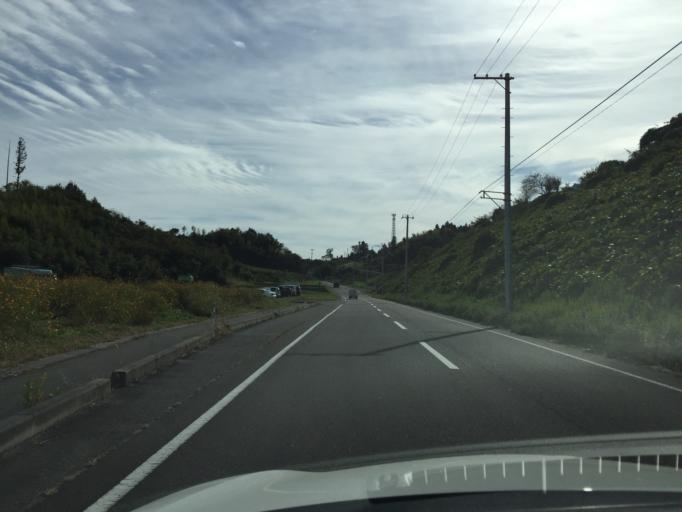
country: JP
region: Fukushima
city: Nihommatsu
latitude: 37.5594
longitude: 140.4997
